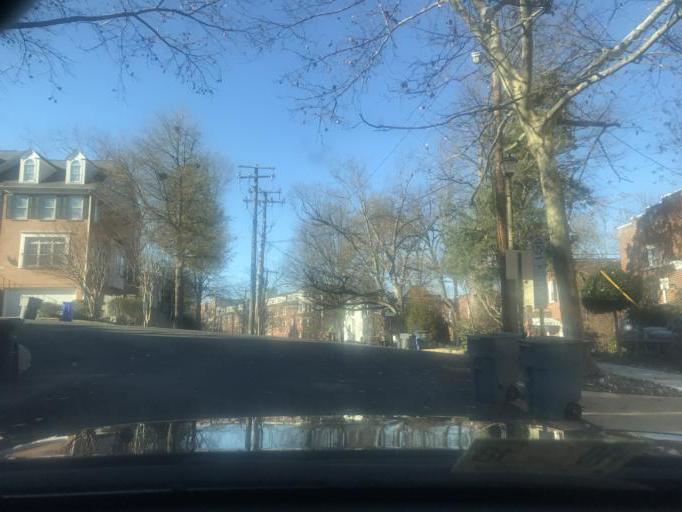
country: US
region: Virginia
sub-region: Arlington County
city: Arlington
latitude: 38.8979
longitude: -77.0759
